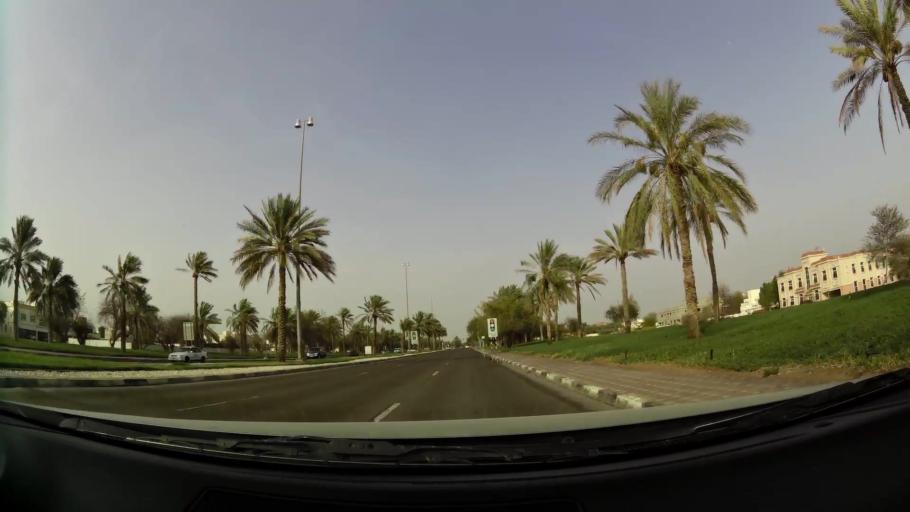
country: AE
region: Abu Dhabi
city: Al Ain
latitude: 24.2207
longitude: 55.6942
